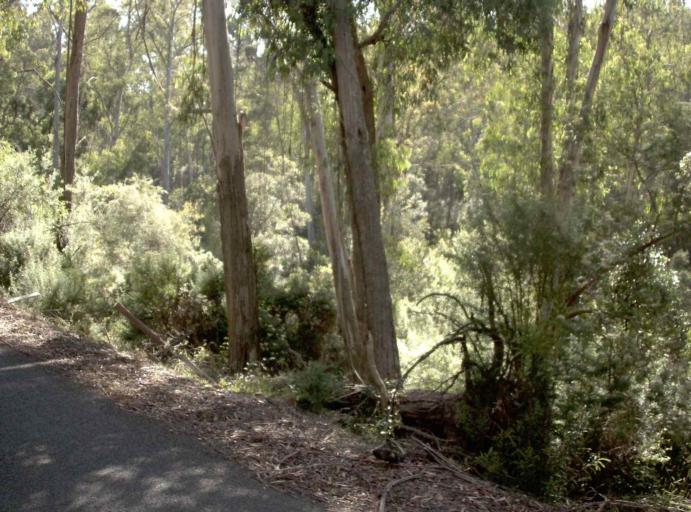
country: AU
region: Victoria
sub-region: East Gippsland
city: Lakes Entrance
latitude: -37.5045
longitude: 148.5415
